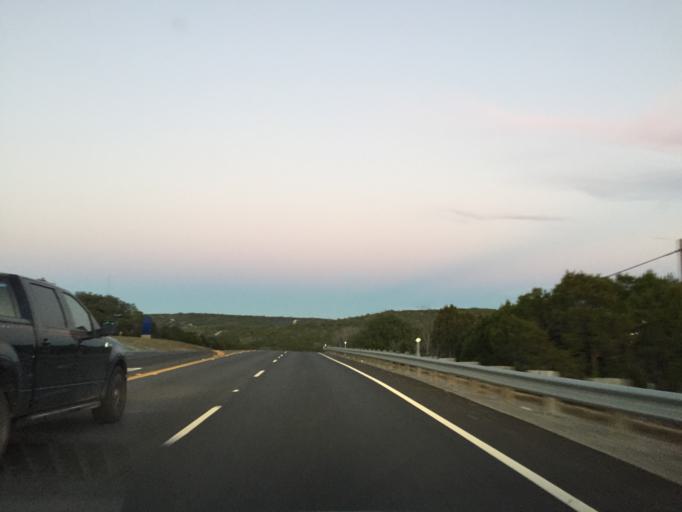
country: US
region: Texas
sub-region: Travis County
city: Jonestown
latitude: 30.5192
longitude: -97.9006
